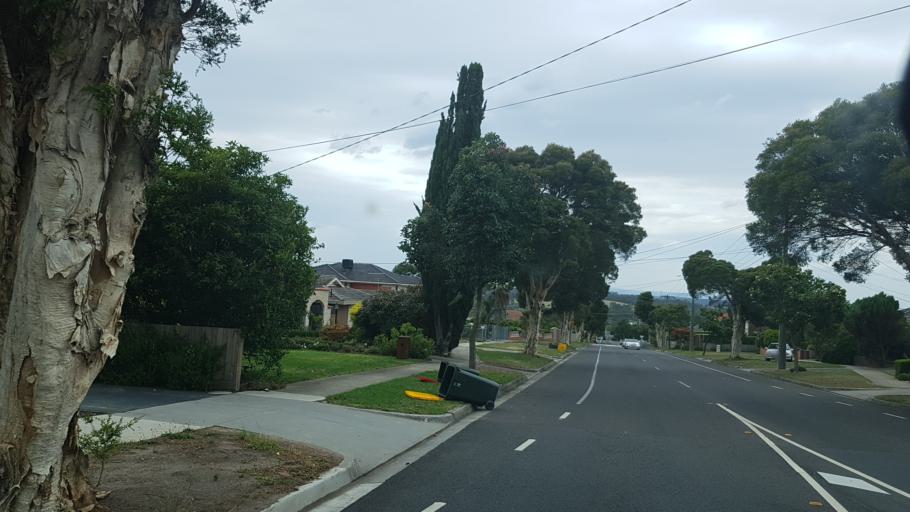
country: AU
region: Victoria
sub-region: Manningham
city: Bulleen
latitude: -37.7635
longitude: 145.0925
